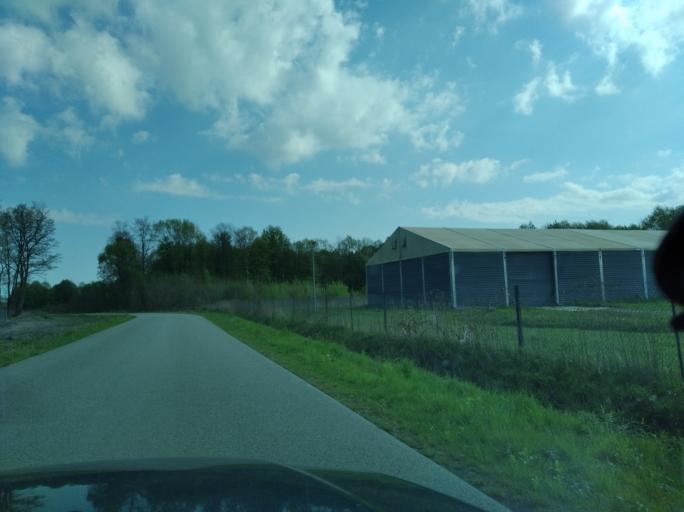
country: PL
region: Subcarpathian Voivodeship
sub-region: Powiat lubaczowski
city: Wielkie Oczy
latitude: 49.9704
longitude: 23.0603
